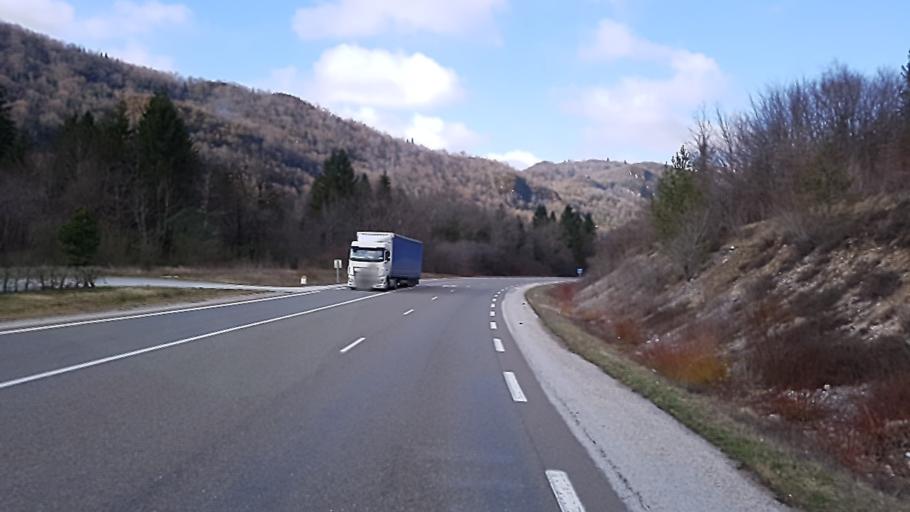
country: FR
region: Rhone-Alpes
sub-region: Departement de l'Ain
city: Dortan
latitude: 46.3508
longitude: 5.6923
